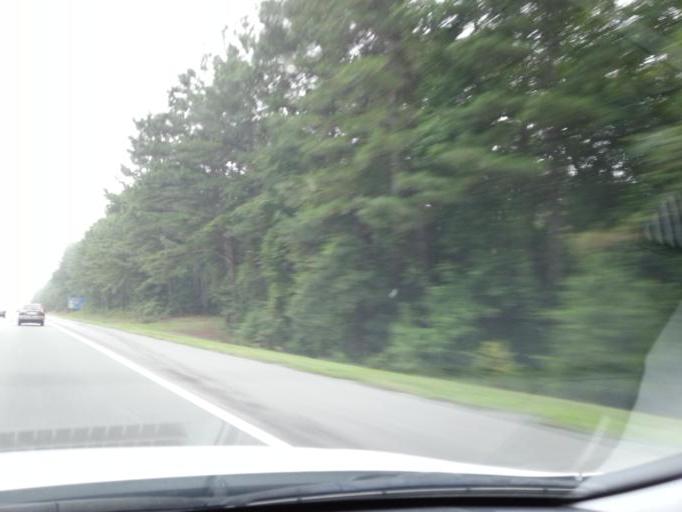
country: US
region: North Carolina
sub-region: Cumberland County
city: Fort Bragg
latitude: 35.0855
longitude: -78.9655
